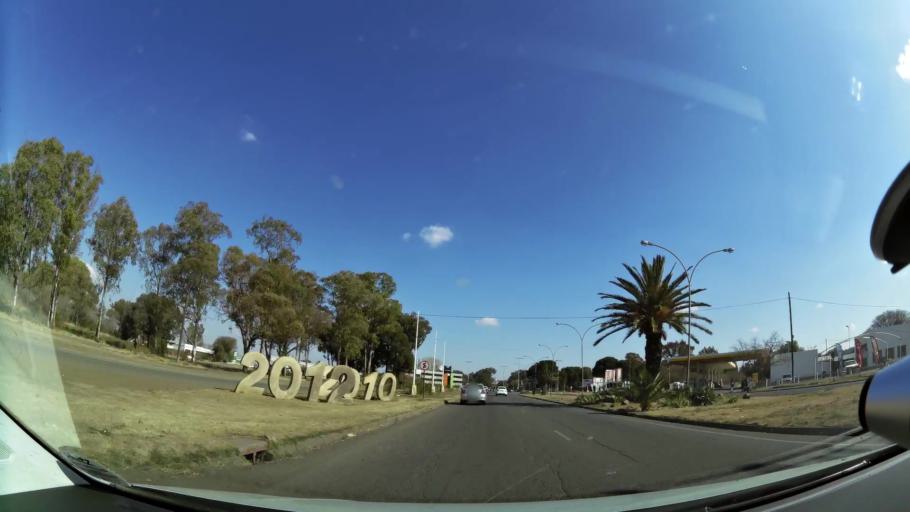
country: ZA
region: Orange Free State
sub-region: Mangaung Metropolitan Municipality
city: Bloemfontein
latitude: -29.1171
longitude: 26.2387
